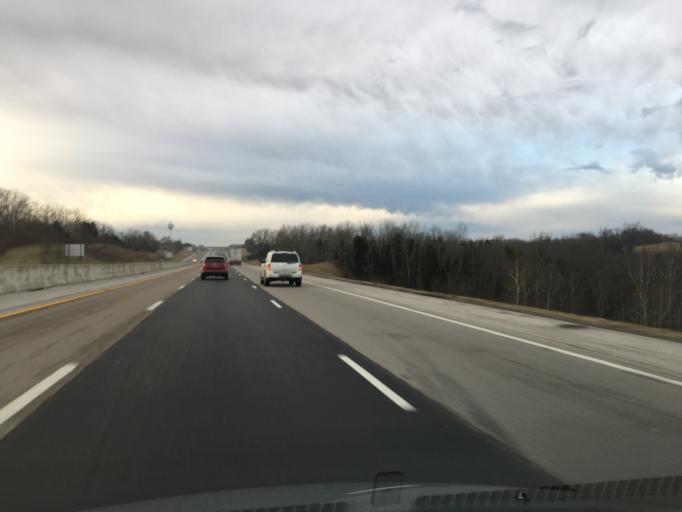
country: US
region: Kentucky
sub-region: Grant County
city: Williamstown
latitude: 38.6172
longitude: -84.5728
